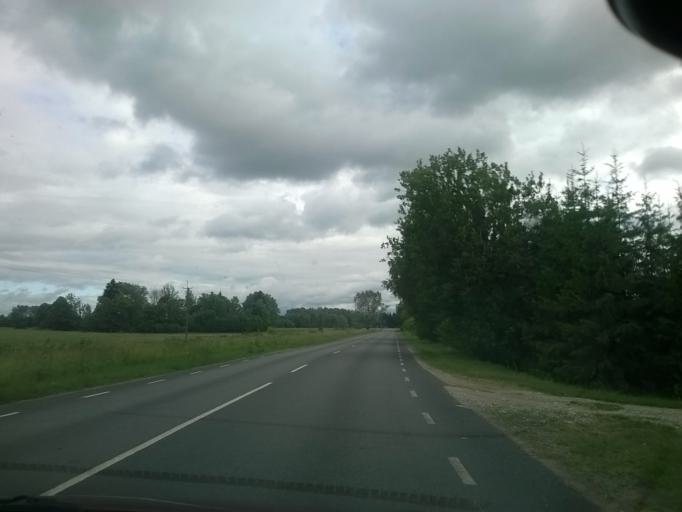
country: EE
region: Laeaene
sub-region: Ridala Parish
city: Uuemoisa
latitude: 58.9609
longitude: 23.7837
